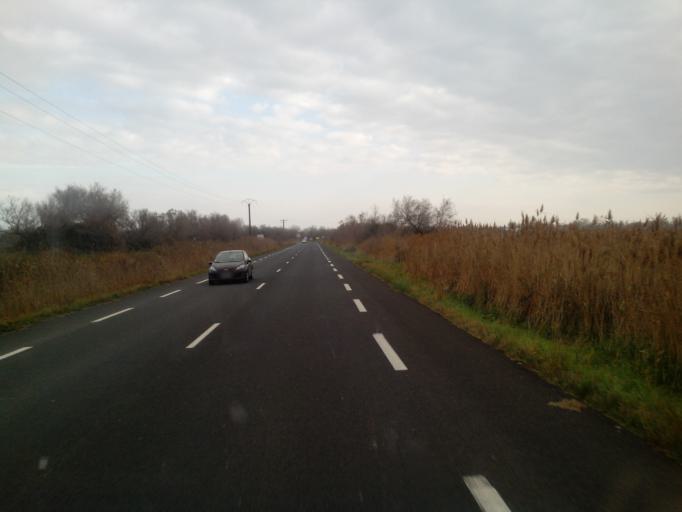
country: FR
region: Provence-Alpes-Cote d'Azur
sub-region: Departement des Bouches-du-Rhone
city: Saintes-Maries-de-la-Mer
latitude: 43.5503
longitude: 4.3388
